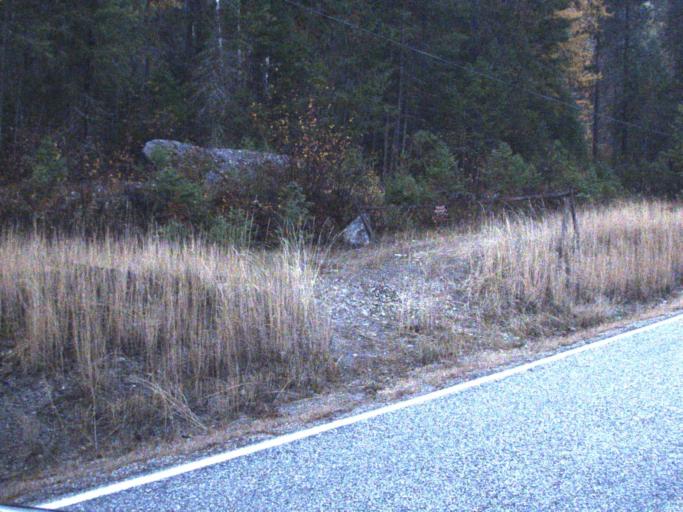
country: CA
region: British Columbia
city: Grand Forks
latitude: 48.9631
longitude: -118.2158
